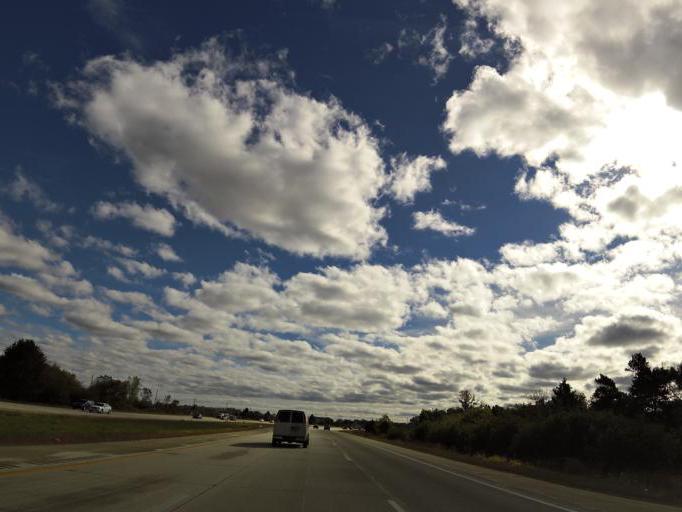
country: US
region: Michigan
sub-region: Genesee County
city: Burton
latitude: 43.0196
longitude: -83.5860
